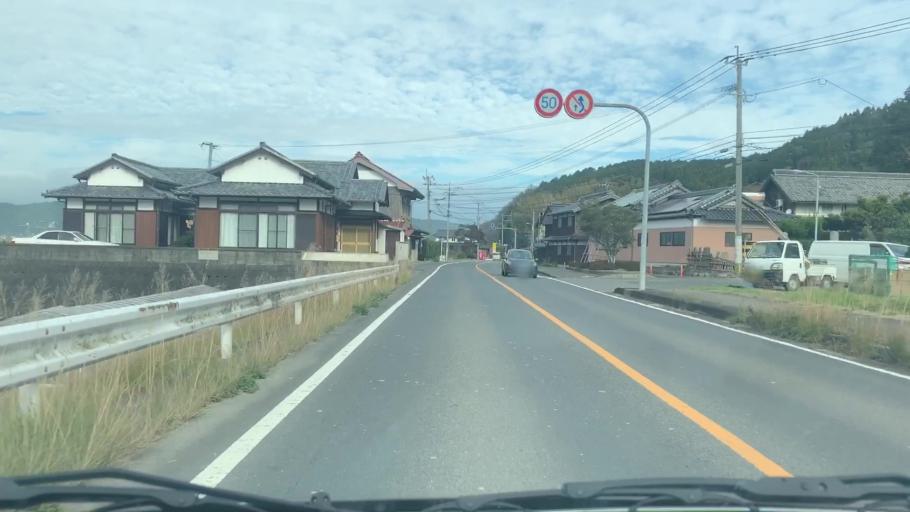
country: JP
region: Saga Prefecture
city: Karatsu
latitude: 33.3874
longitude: 129.9879
